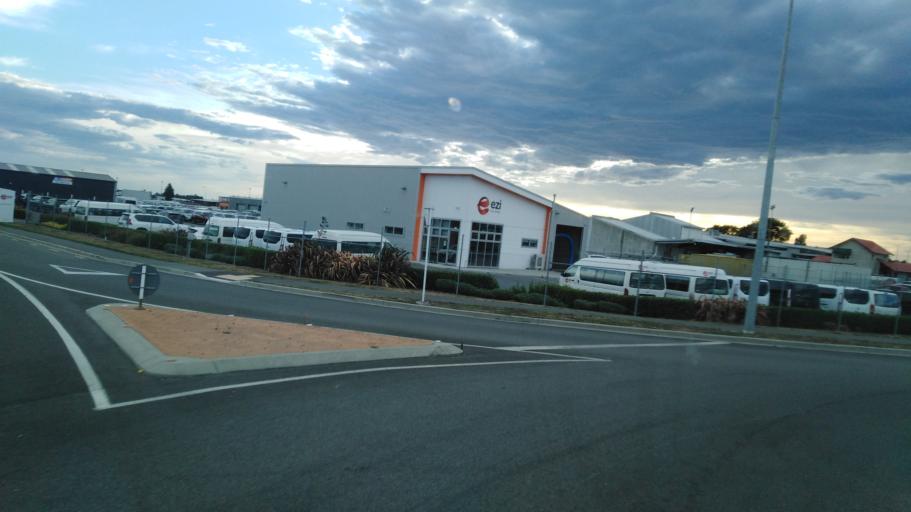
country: NZ
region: Canterbury
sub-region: Christchurch City
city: Christchurch
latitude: -43.4778
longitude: 172.5534
